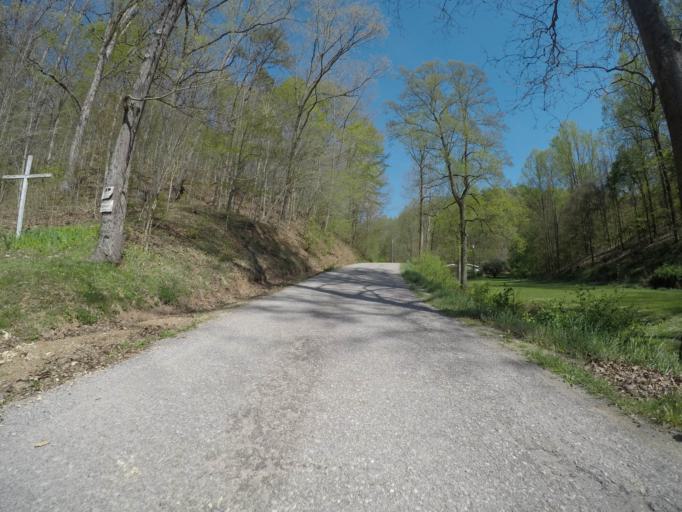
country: US
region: West Virginia
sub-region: Kanawha County
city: Charleston
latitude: 38.4122
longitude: -81.6010
